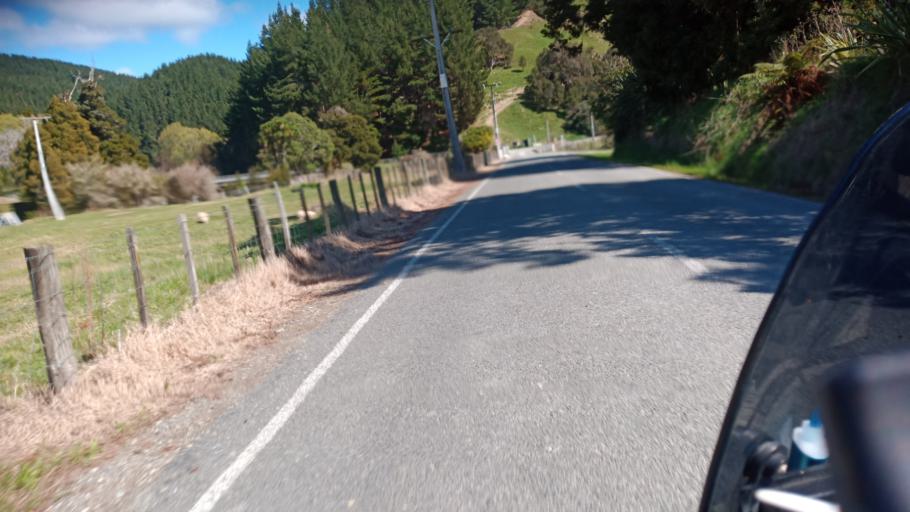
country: NZ
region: Gisborne
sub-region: Gisborne District
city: Gisborne
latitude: -38.7872
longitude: 177.7945
